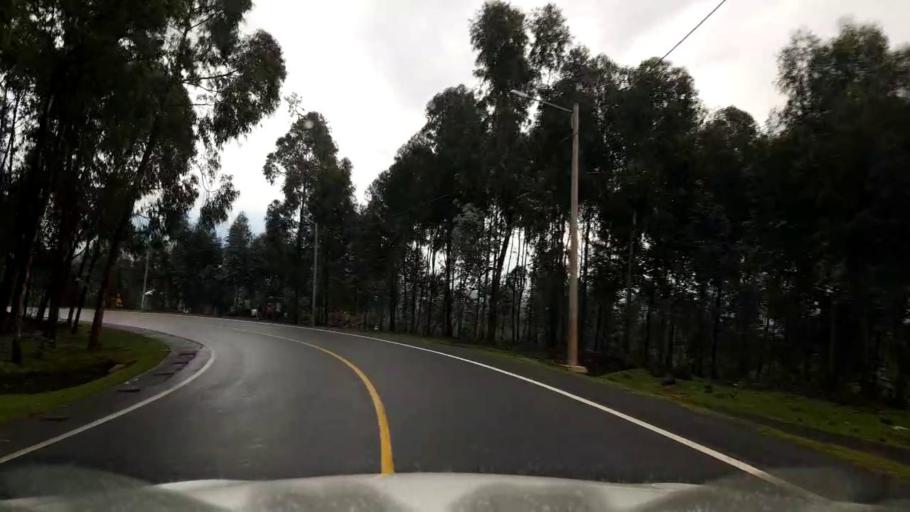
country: RW
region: Northern Province
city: Musanze
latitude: -1.5138
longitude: 29.5979
